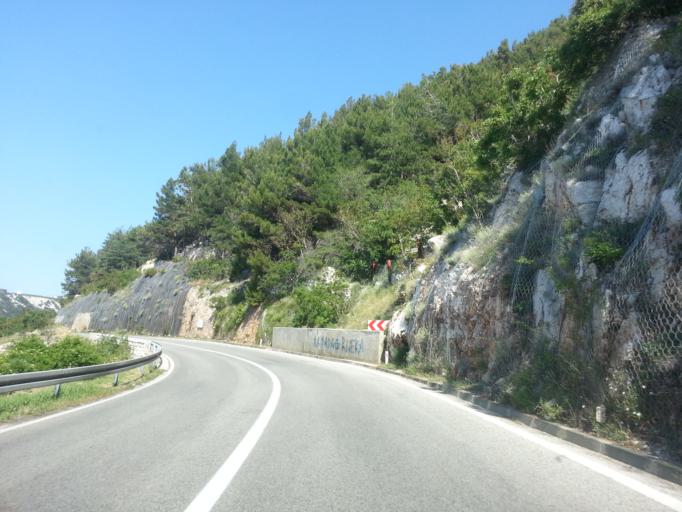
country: HR
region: Primorsko-Goranska
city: Kraljevica
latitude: 45.2929
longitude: 14.5696
